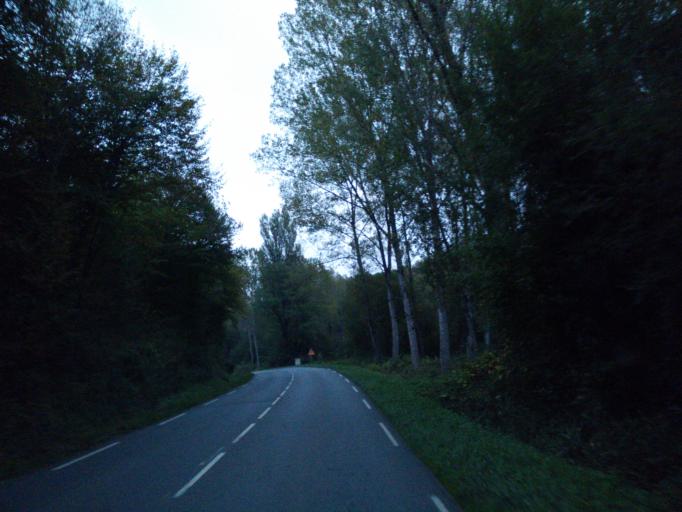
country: FR
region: Aquitaine
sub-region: Departement de la Dordogne
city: Sarlat-la-Caneda
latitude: 44.9062
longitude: 1.1289
